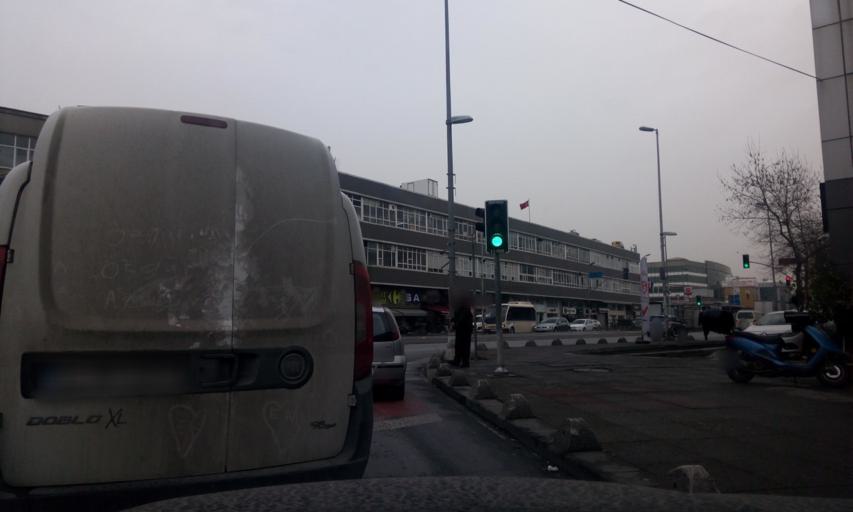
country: TR
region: Istanbul
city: Esenler
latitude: 41.0427
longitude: 28.9182
